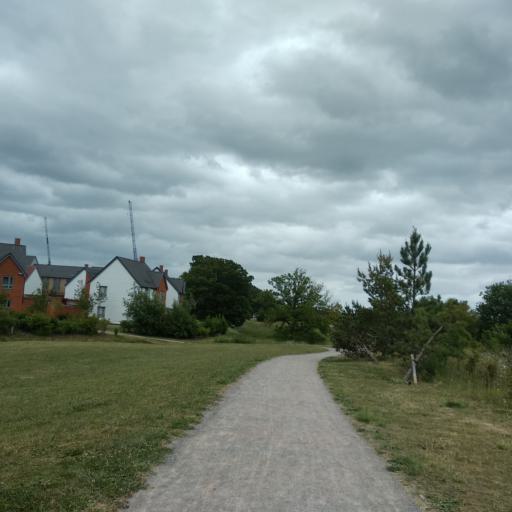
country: GB
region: England
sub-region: Kent
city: Ashford
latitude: 51.1577
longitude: 0.8495
